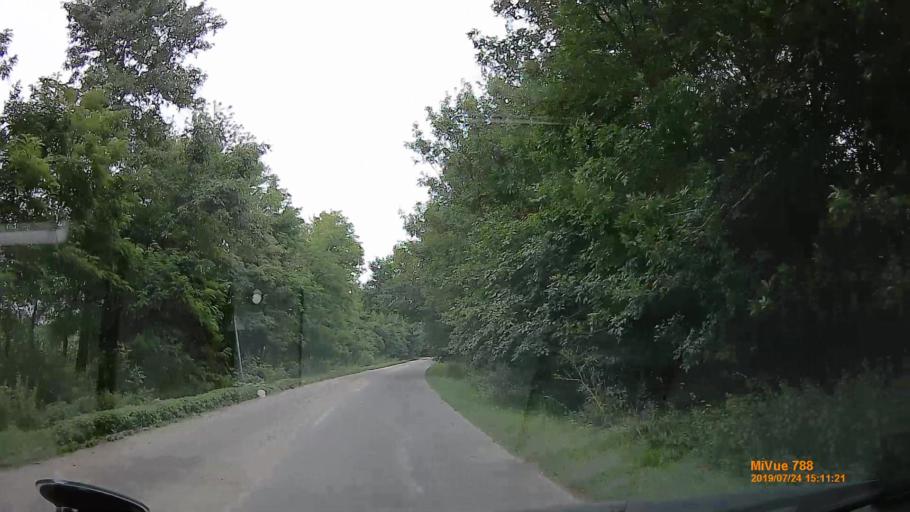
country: HU
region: Szabolcs-Szatmar-Bereg
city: Tarpa
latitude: 48.2022
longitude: 22.4763
